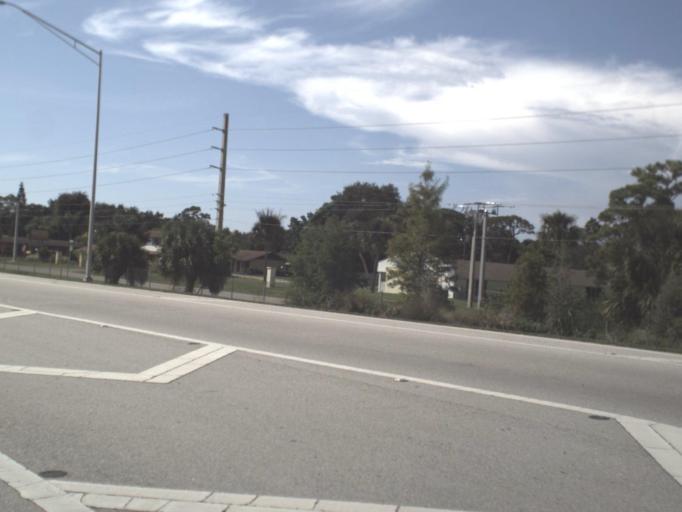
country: US
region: Florida
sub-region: Sarasota County
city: Laurel
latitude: 27.1449
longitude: -82.4621
